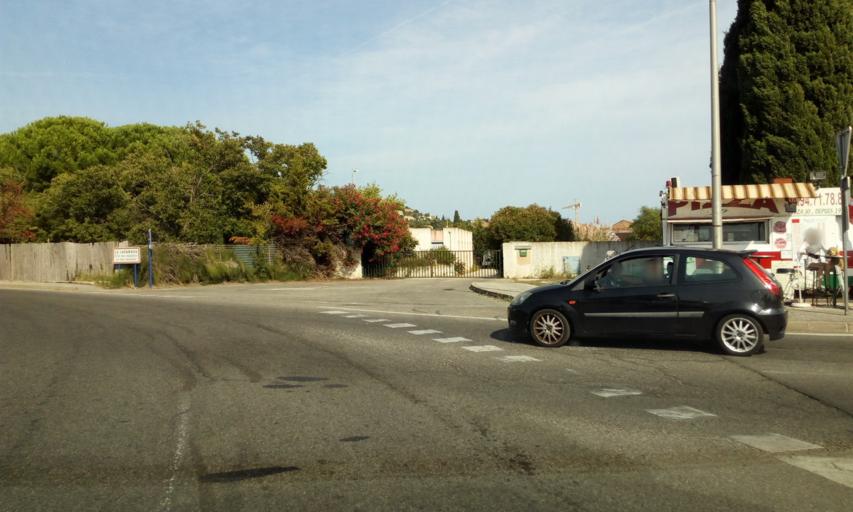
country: FR
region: Provence-Alpes-Cote d'Azur
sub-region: Departement du Var
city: Bormes-les-Mimosas
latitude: 43.1385
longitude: 6.3517
